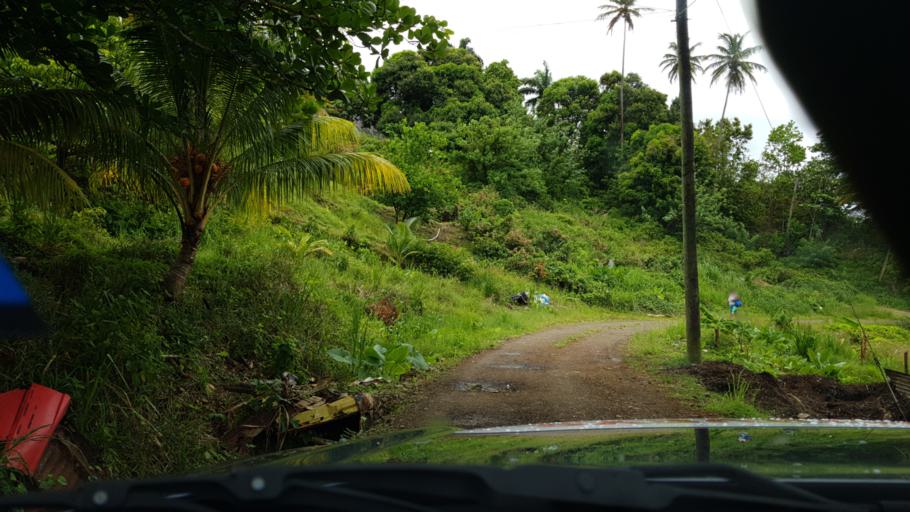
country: LC
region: Anse-la-Raye
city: Anse La Raye
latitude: 13.9442
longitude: -60.9925
